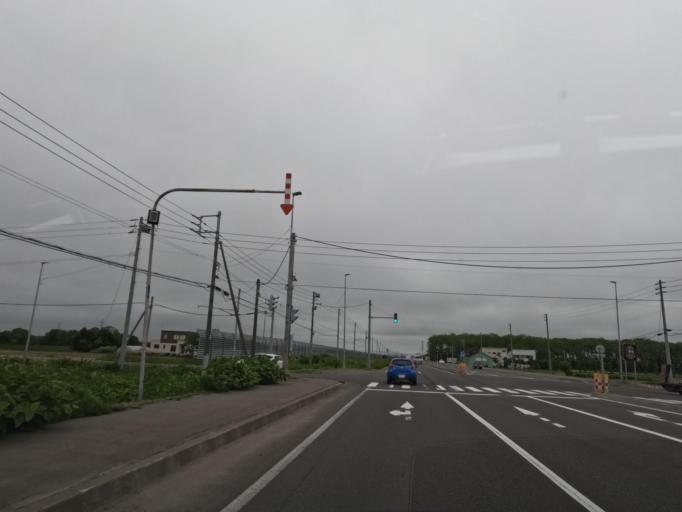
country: JP
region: Hokkaido
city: Ebetsu
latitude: 43.1492
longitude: 141.5176
